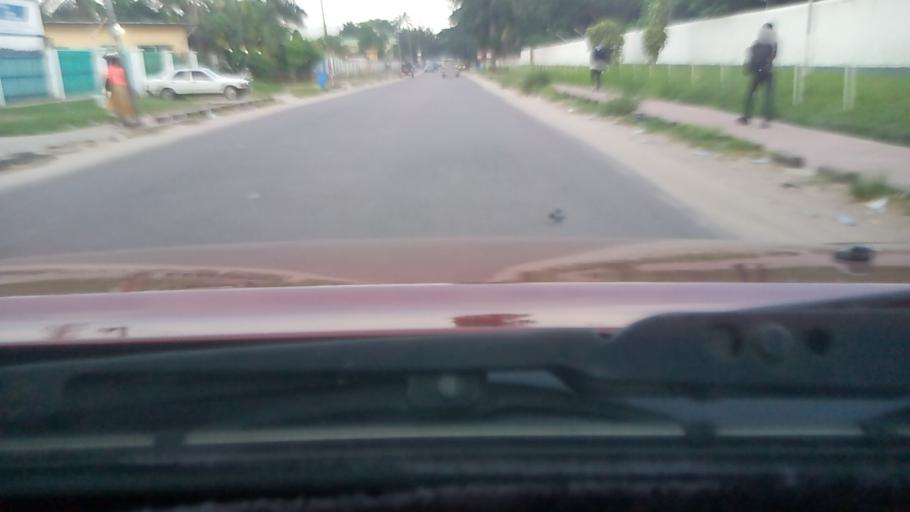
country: CD
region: Kinshasa
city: Kinshasa
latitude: -4.3098
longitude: 15.2827
